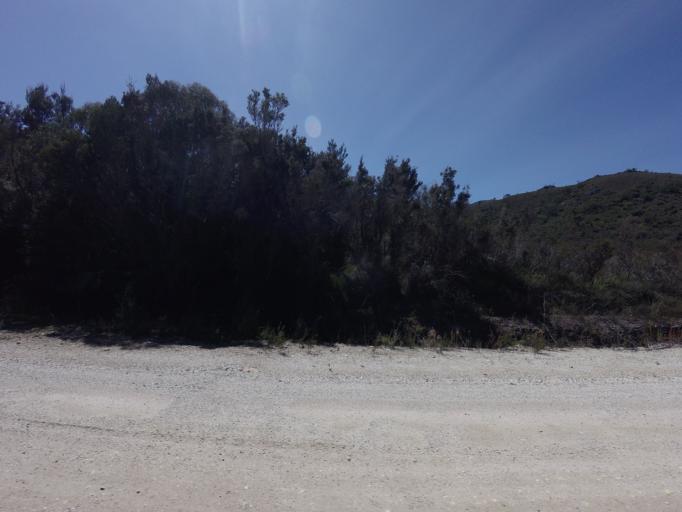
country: AU
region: Tasmania
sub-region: Huon Valley
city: Geeveston
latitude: -42.9470
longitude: 146.3519
